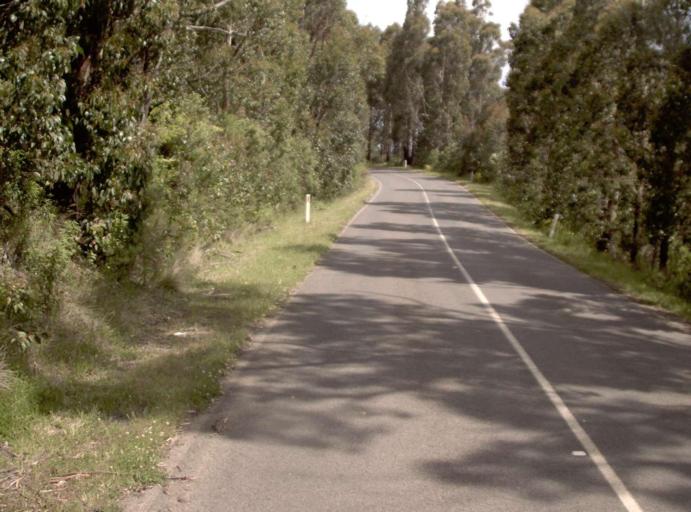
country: AU
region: Victoria
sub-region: Latrobe
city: Traralgon
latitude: -38.3929
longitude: 146.5553
